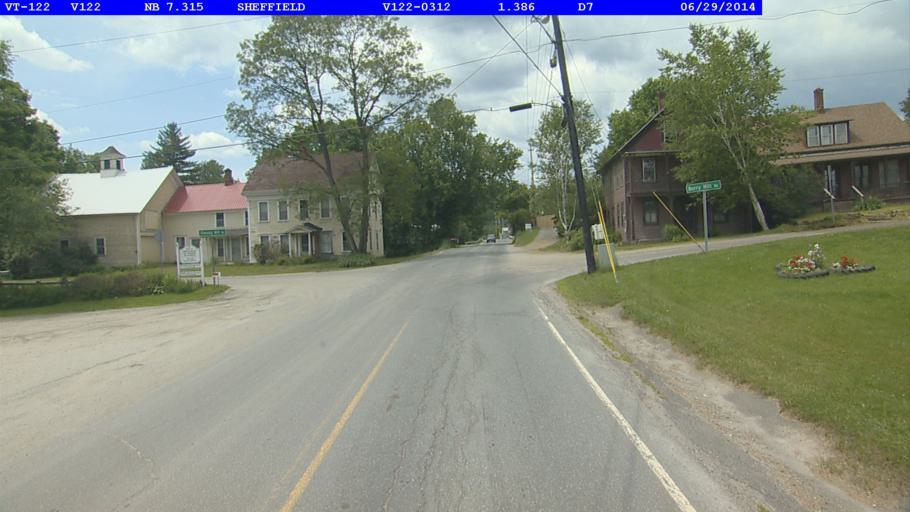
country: US
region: Vermont
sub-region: Caledonia County
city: Lyndonville
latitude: 44.6018
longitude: -72.1140
